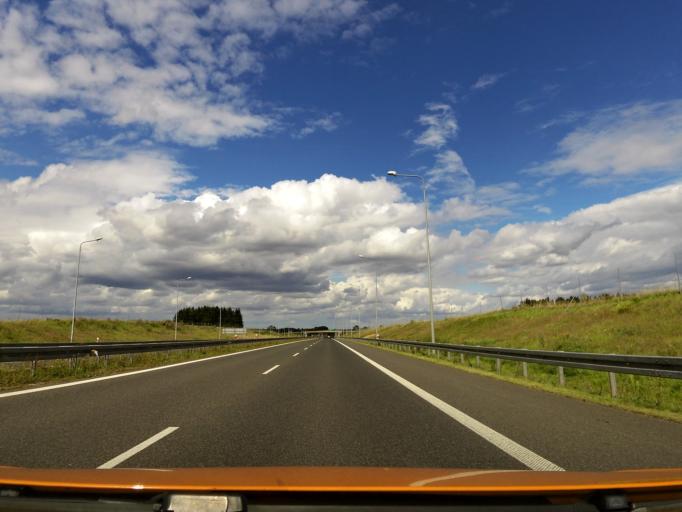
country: PL
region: West Pomeranian Voivodeship
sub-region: Powiat goleniowski
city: Nowogard
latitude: 53.6805
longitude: 15.0854
